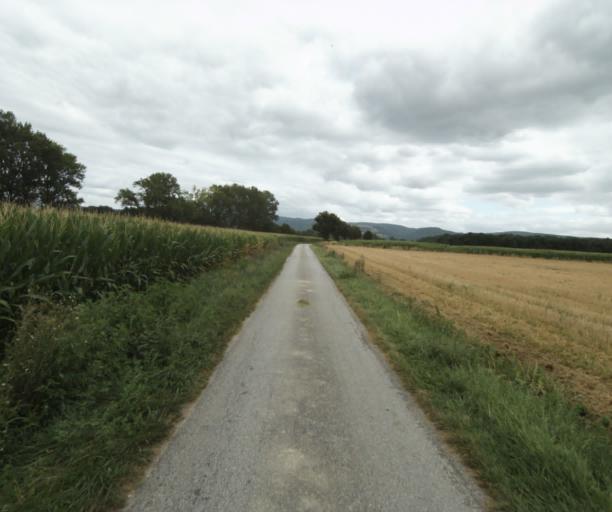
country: FR
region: Midi-Pyrenees
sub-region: Departement de la Haute-Garonne
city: Revel
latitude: 43.4879
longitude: 2.0383
